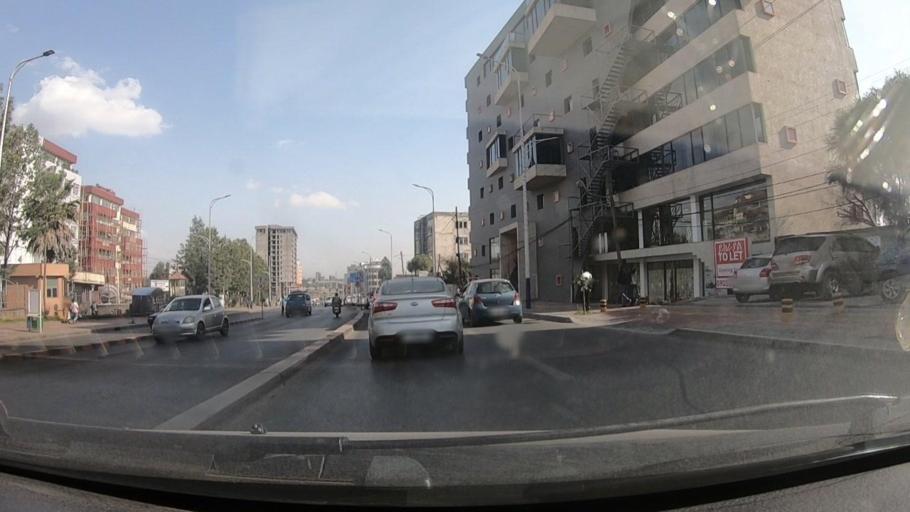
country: ET
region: Adis Abeba
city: Addis Ababa
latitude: 8.9911
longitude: 38.7402
